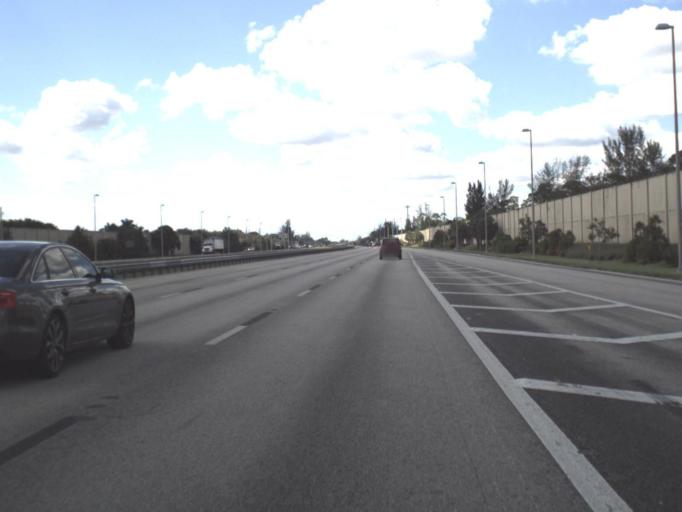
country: US
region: Florida
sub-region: Broward County
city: Parkland
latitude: 26.3005
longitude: -80.2089
